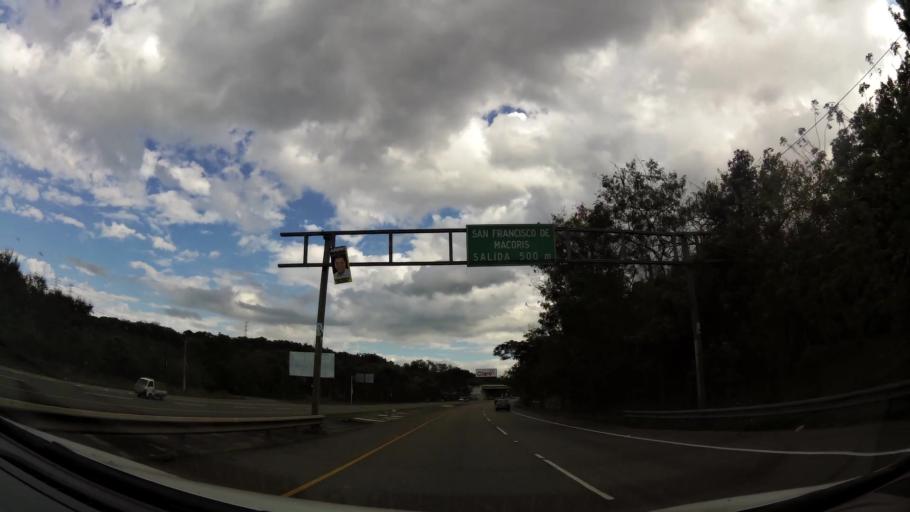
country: DO
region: La Vega
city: Rincon
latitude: 19.1357
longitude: -70.4604
